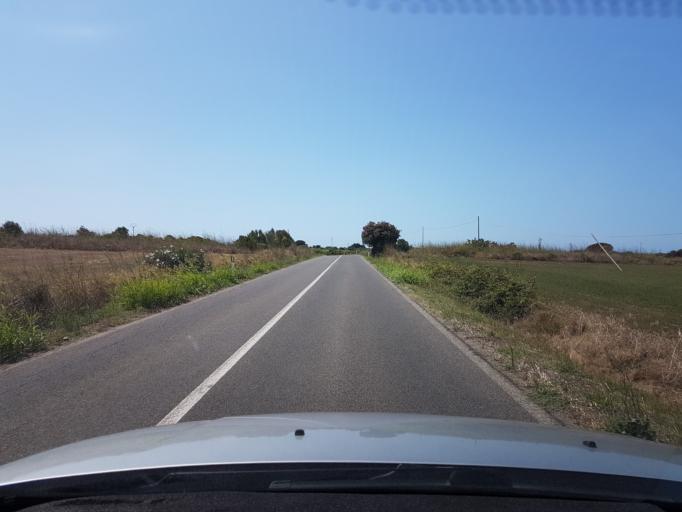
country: IT
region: Sardinia
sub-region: Provincia di Oristano
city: Riola Sardo
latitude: 40.0223
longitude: 8.4760
